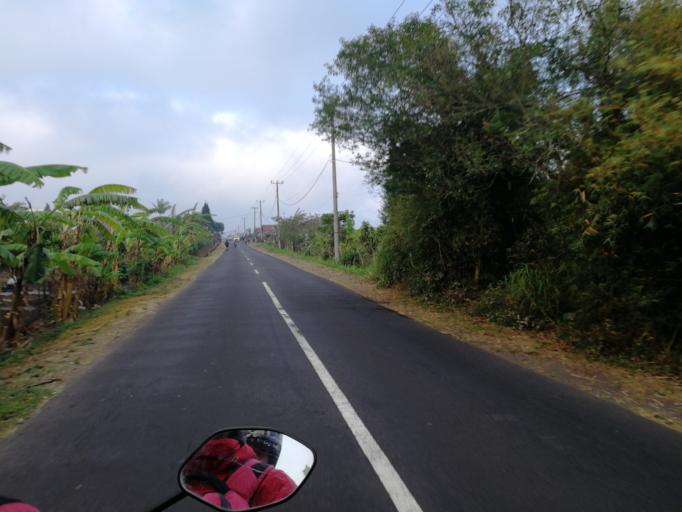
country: ID
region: Bali
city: Banjar Kedisan
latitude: -8.2218
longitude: 115.2668
